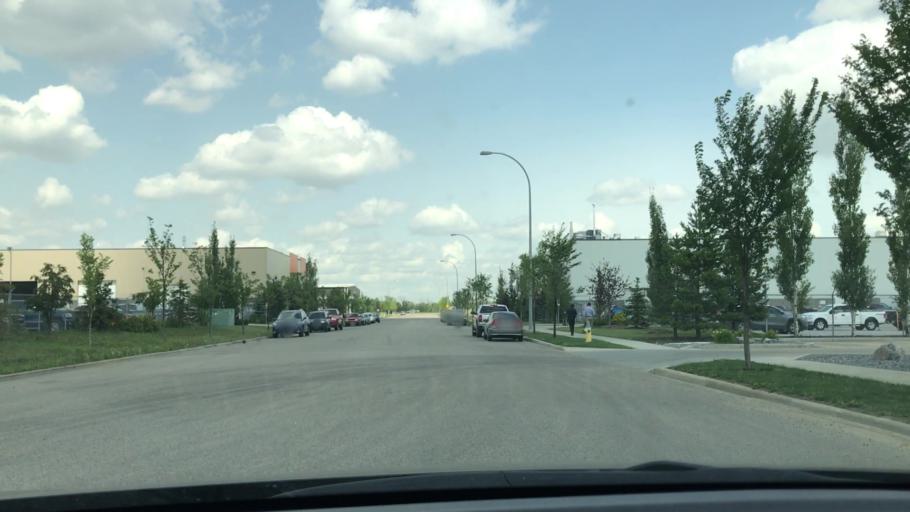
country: CA
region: Alberta
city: Edmonton
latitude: 53.4936
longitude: -113.4060
